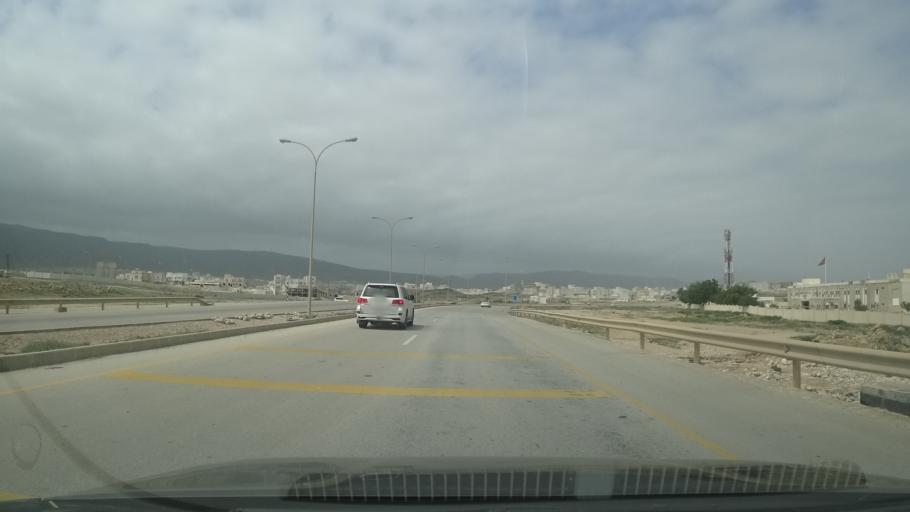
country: OM
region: Zufar
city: Salalah
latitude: 17.0493
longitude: 54.3857
